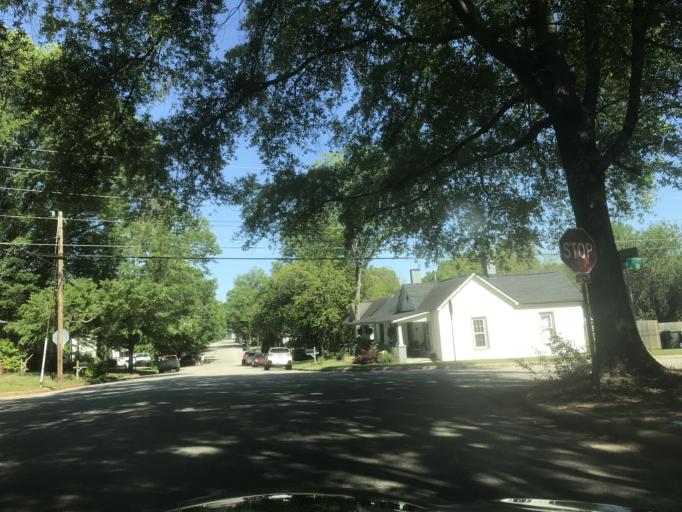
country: US
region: North Carolina
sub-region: Wake County
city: Raleigh
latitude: 35.7608
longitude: -78.6482
